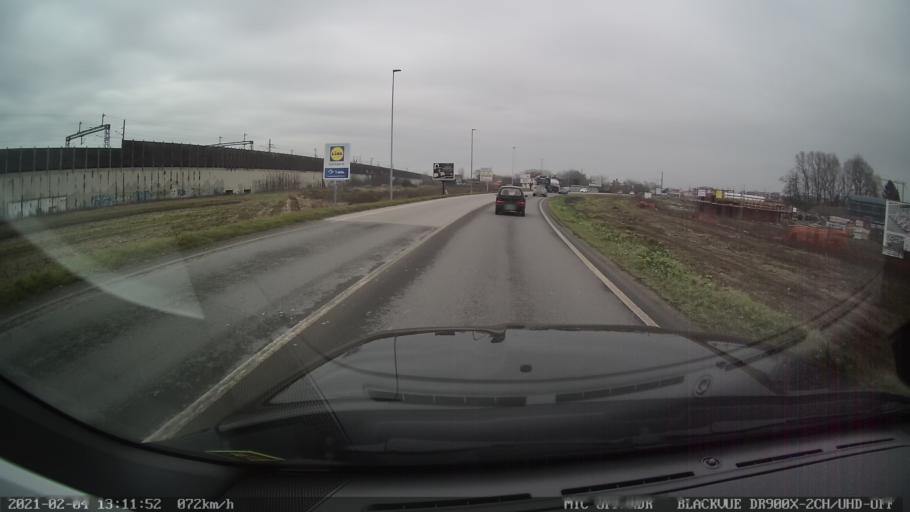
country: IT
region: Piedmont
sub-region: Provincia di Novara
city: Novara
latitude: 45.4694
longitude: 8.6200
